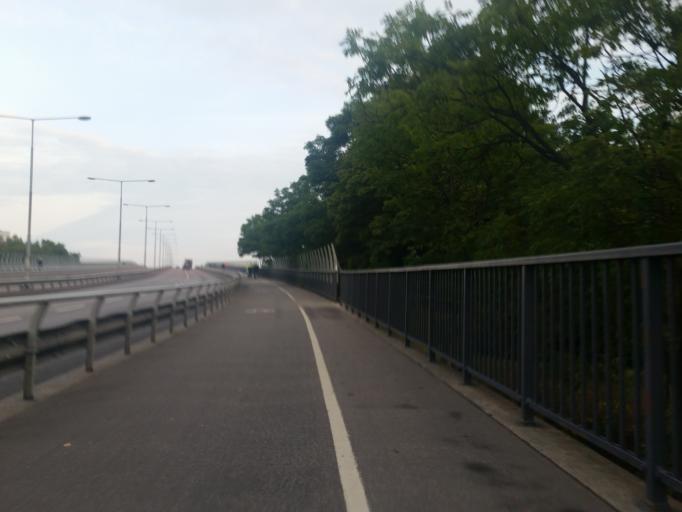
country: SE
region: Stockholm
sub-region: Stockholms Kommun
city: Arsta
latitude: 59.3217
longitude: 18.0307
